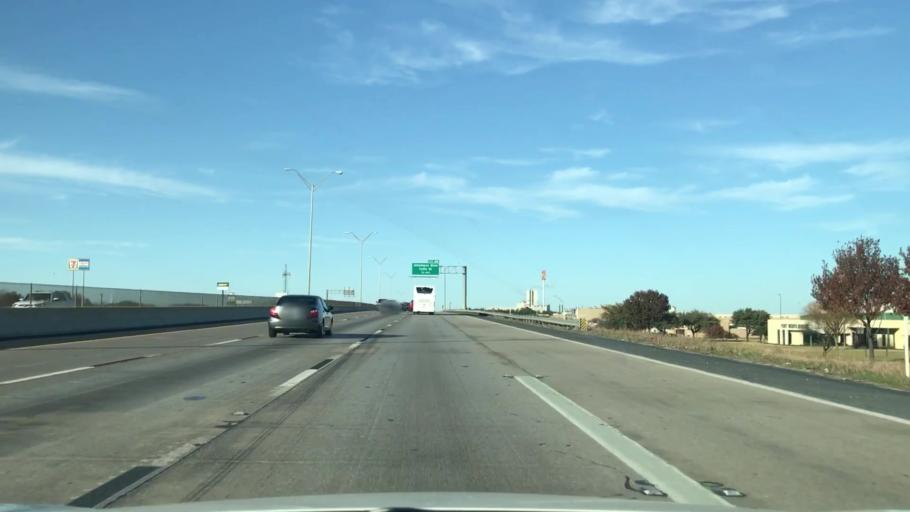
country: US
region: Texas
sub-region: Tarrant County
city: Everman
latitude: 32.6326
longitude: -97.3214
